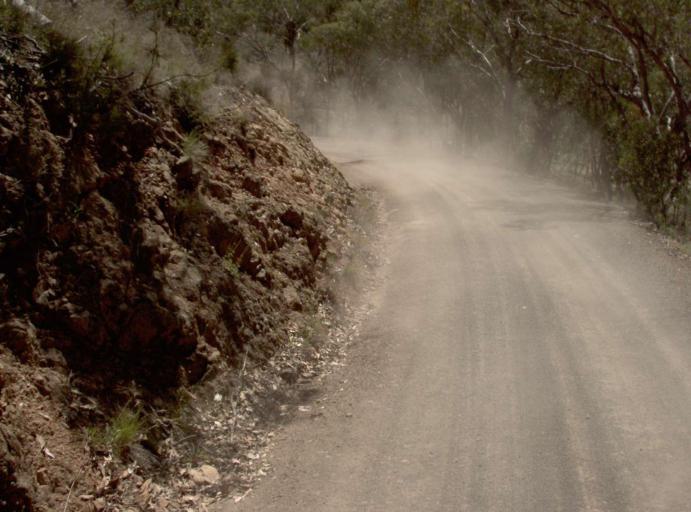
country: AU
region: New South Wales
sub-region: Snowy River
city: Jindabyne
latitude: -37.0793
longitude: 148.4584
